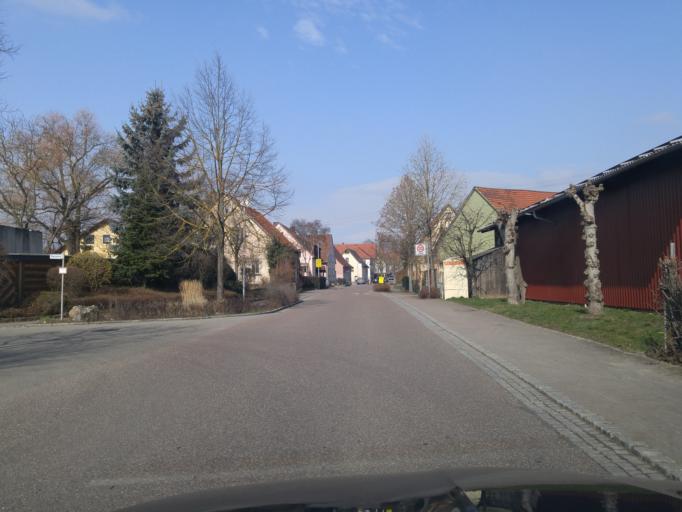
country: DE
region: Baden-Wuerttemberg
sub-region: Regierungsbezirk Stuttgart
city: Abstatt
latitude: 49.0562
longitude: 9.2830
